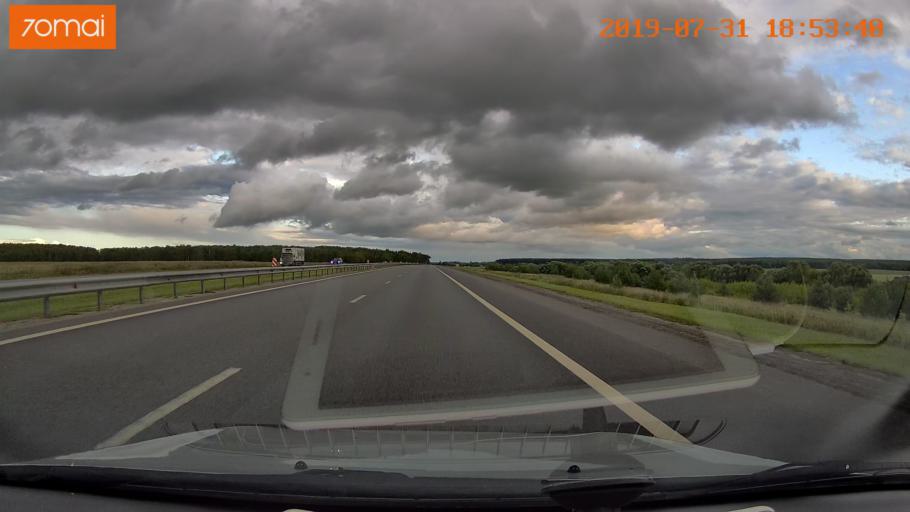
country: RU
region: Moskovskaya
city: Raduzhnyy
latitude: 55.2000
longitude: 38.6577
